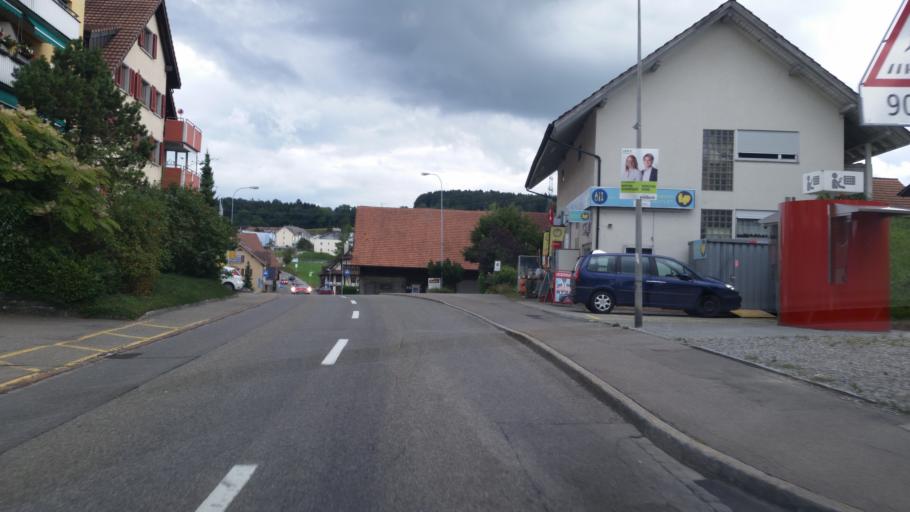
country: CH
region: Aargau
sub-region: Bezirk Bremgarten
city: Oberlunkhofen
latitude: 47.3183
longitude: 8.4194
